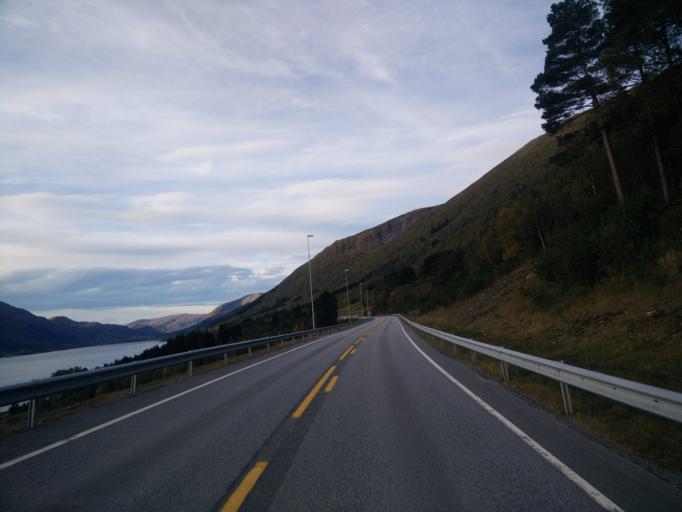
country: NO
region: More og Romsdal
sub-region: Gjemnes
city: Batnfjordsora
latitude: 62.9522
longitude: 7.7653
